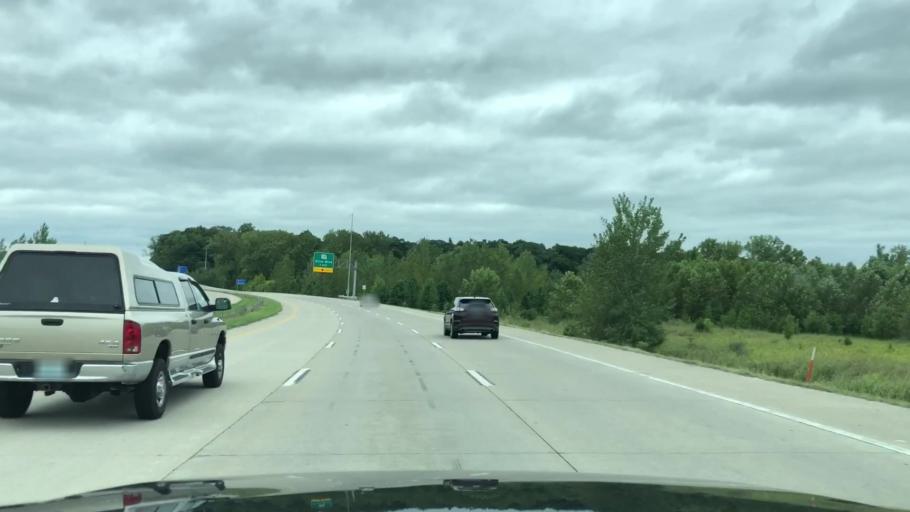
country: US
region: Missouri
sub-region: Saint Louis County
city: Maryland Heights
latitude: 38.6976
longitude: -90.5031
